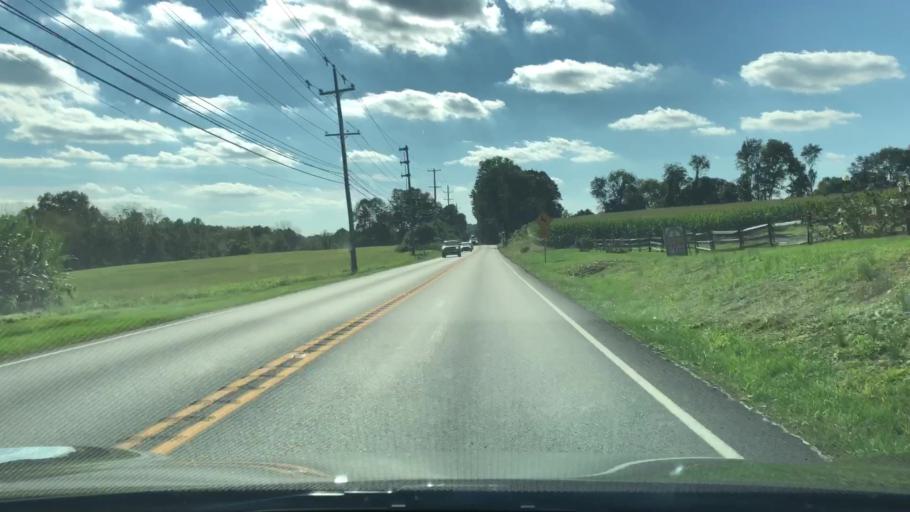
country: US
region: Pennsylvania
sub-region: Chester County
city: West Chester
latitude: 39.9387
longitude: -75.5355
